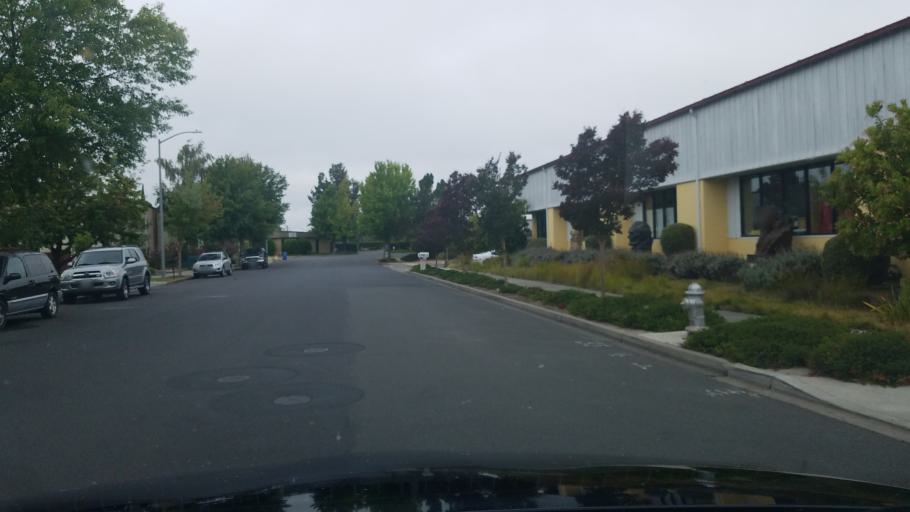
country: US
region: California
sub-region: Napa County
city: Napa
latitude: 38.2590
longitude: -122.2749
